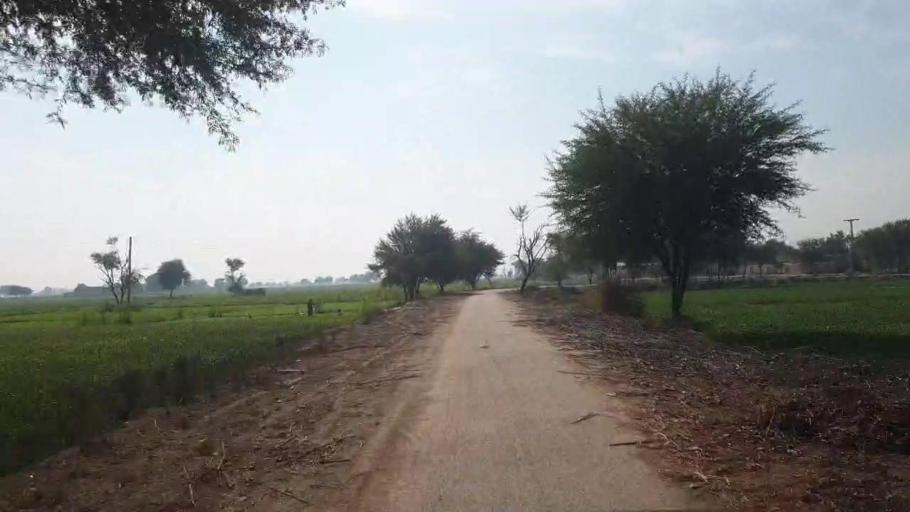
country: PK
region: Sindh
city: Nawabshah
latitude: 26.1614
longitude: 68.4951
